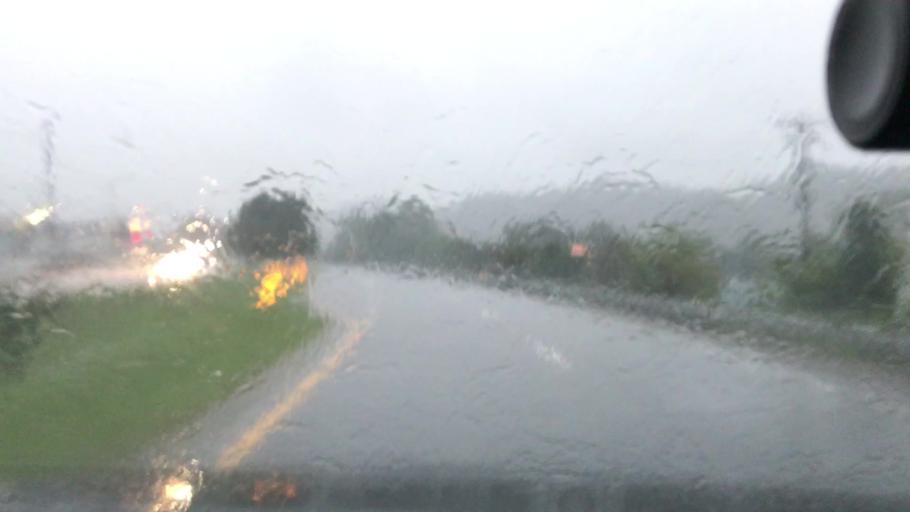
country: US
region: Virginia
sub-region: Giles County
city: Narrows
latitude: 37.3345
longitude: -80.8028
